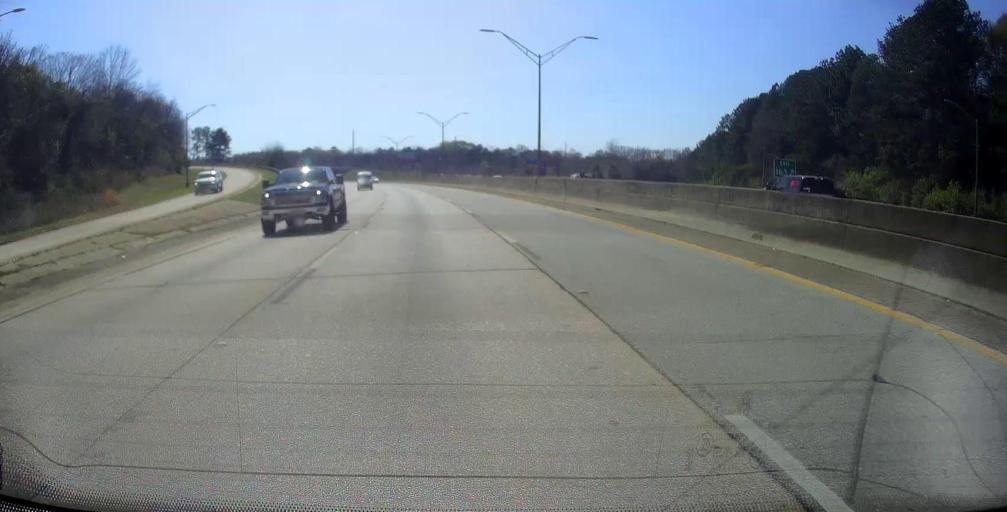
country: US
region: Georgia
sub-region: Bibb County
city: Macon
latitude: 32.8275
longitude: -83.6582
